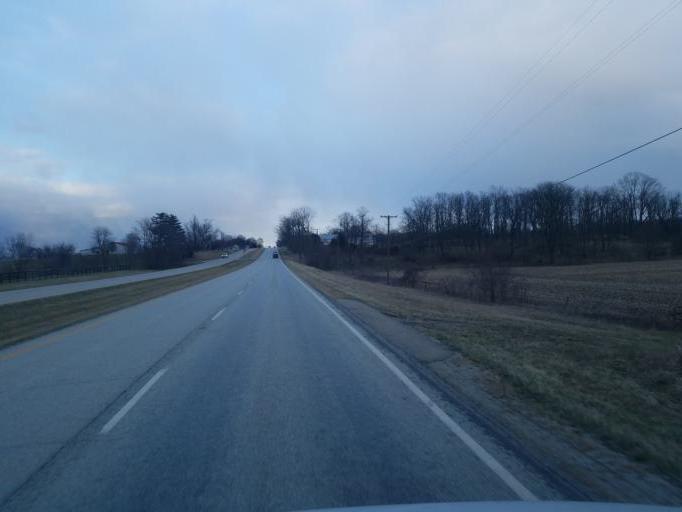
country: US
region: Indiana
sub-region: Hancock County
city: Greenfield
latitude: 39.7899
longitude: -85.6567
